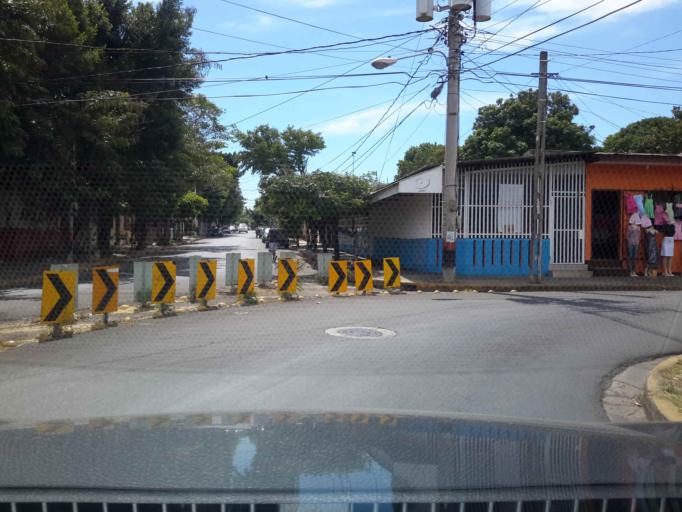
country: NI
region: Managua
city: Managua
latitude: 12.1338
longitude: -86.2930
